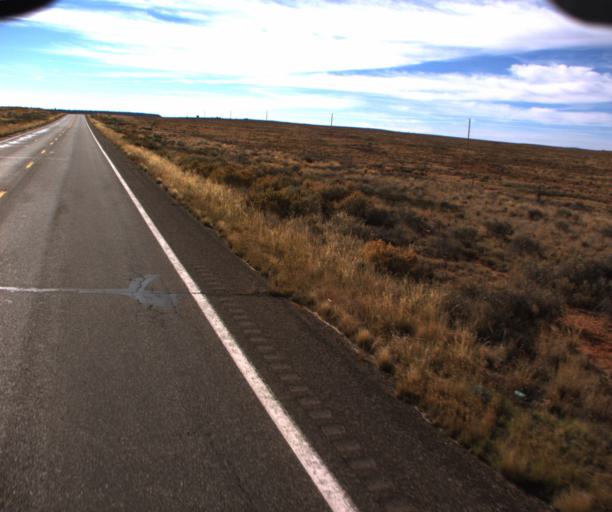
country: US
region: Arizona
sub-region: Coconino County
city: Kaibito
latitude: 36.7095
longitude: -111.2704
